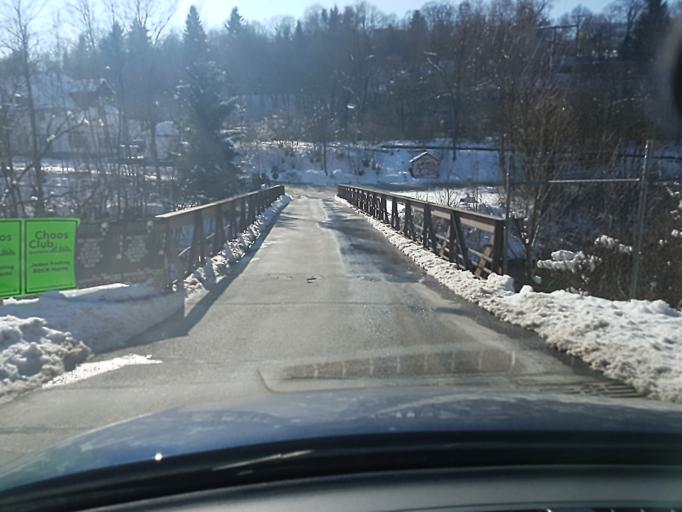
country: DE
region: Baden-Wuerttemberg
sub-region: Freiburg Region
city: Rottweil
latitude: 48.1753
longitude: 8.6286
